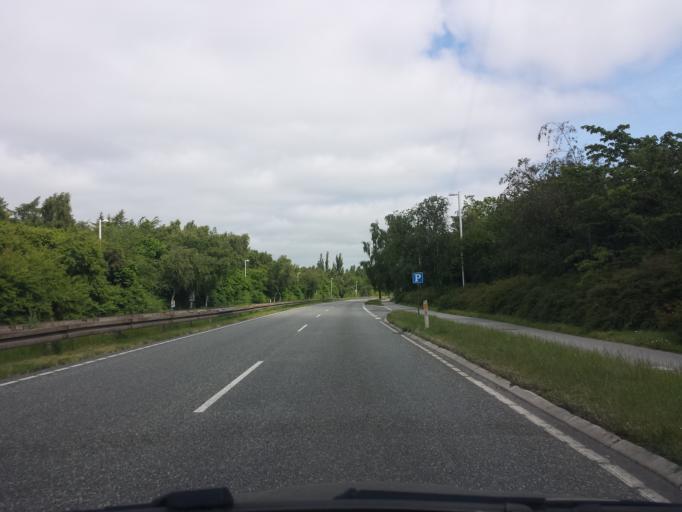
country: DK
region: Capital Region
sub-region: Glostrup Kommune
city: Glostrup
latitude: 55.6794
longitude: 12.3966
